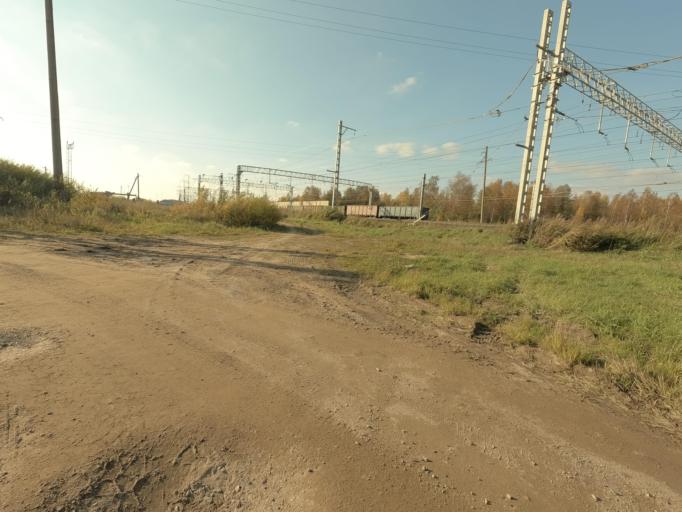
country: RU
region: Leningrad
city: Mga
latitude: 59.7544
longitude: 31.0911
